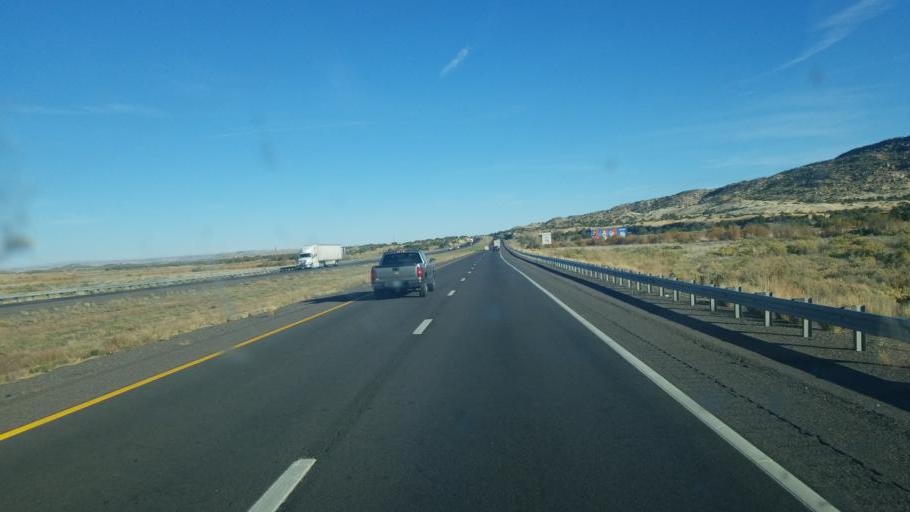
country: US
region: New Mexico
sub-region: Cibola County
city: Laguna
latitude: 35.0327
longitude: -107.4682
